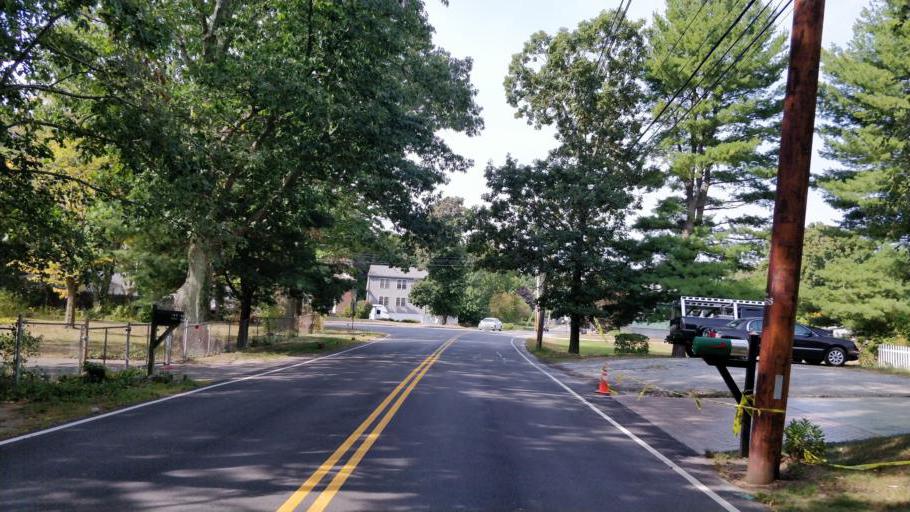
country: US
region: Massachusetts
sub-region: Bristol County
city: North Seekonk
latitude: 41.9035
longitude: -71.3301
